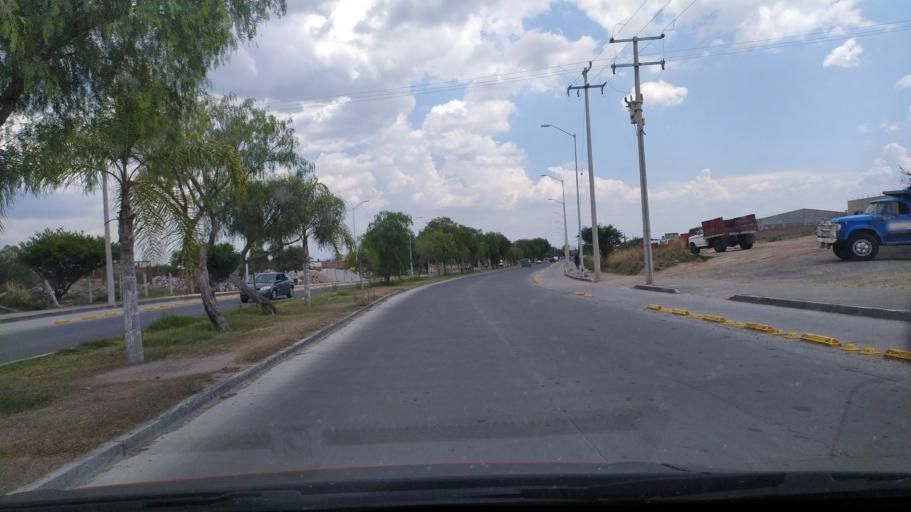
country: MX
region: Guanajuato
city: San Francisco del Rincon
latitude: 21.0430
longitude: -101.8692
